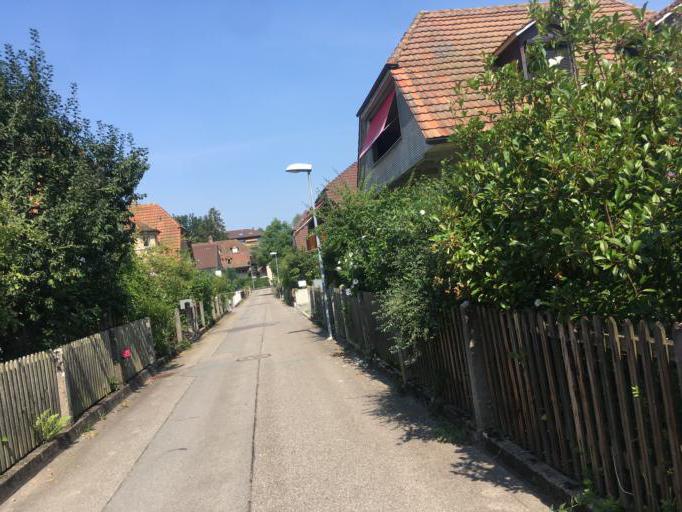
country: CH
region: Bern
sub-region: Bern-Mittelland District
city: Muri
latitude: 46.9405
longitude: 7.4990
